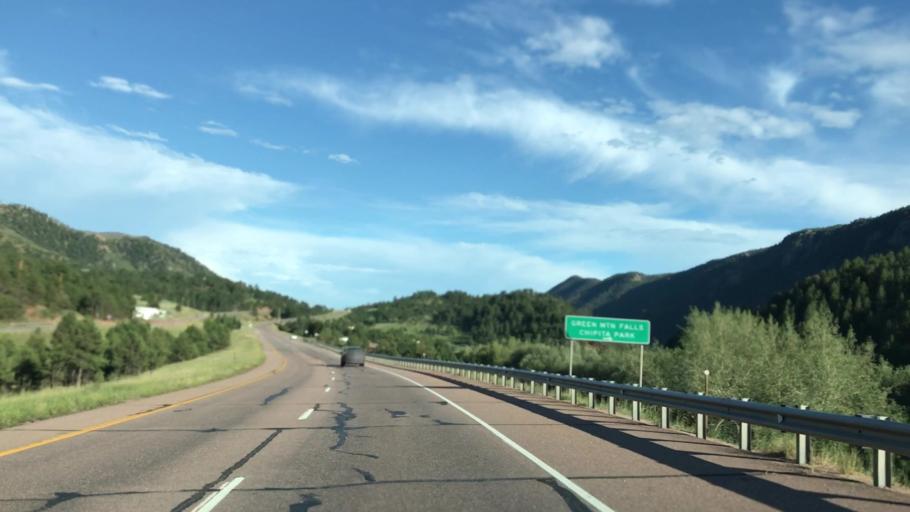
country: US
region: Colorado
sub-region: El Paso County
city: Cascade-Chipita Park
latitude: 38.9438
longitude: -105.0197
